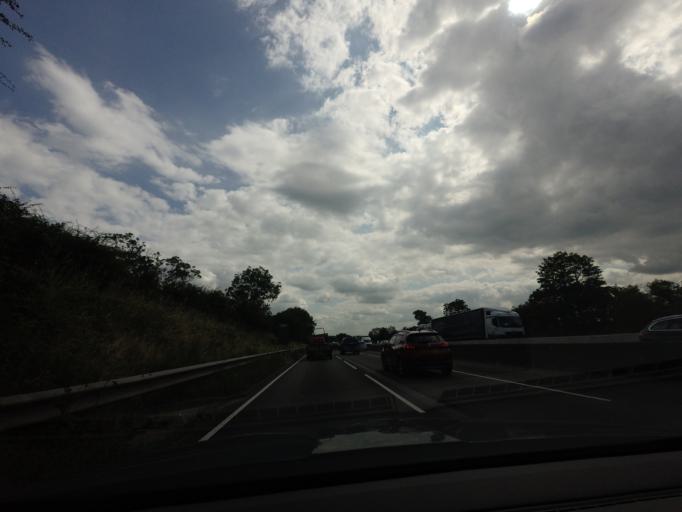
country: GB
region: England
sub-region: Staffordshire
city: Stone
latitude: 52.8606
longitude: -2.1630
